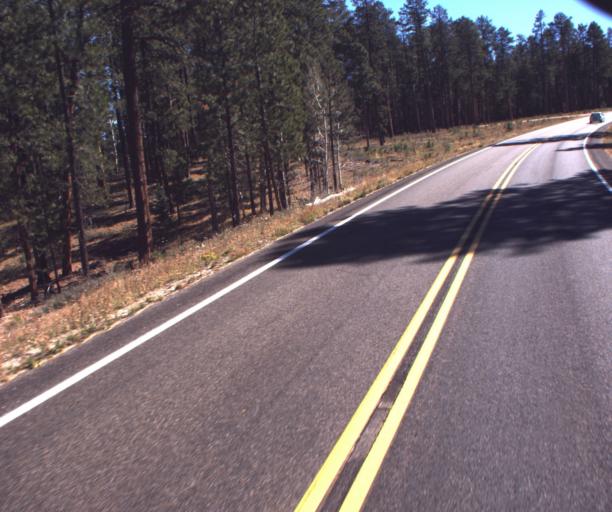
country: US
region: Arizona
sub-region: Coconino County
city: Fredonia
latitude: 36.6651
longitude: -112.1927
